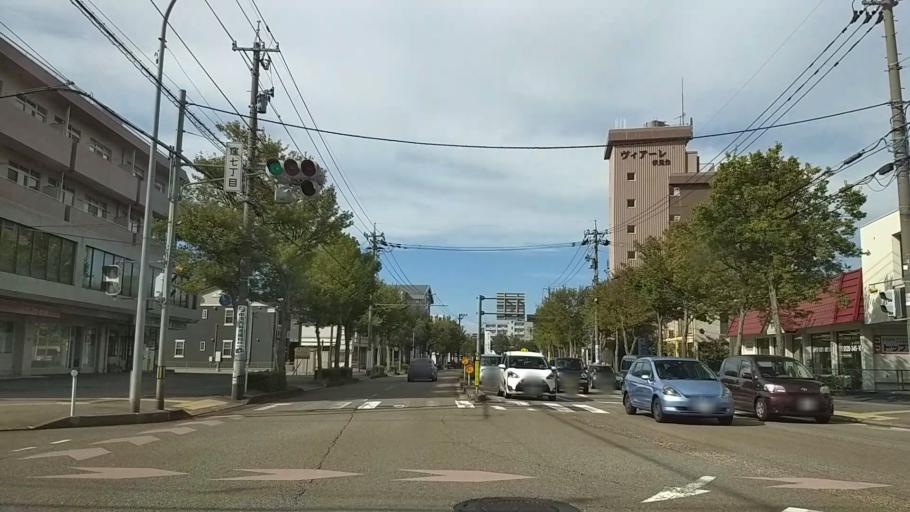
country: JP
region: Ishikawa
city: Nonoichi
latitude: 36.5291
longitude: 136.6382
